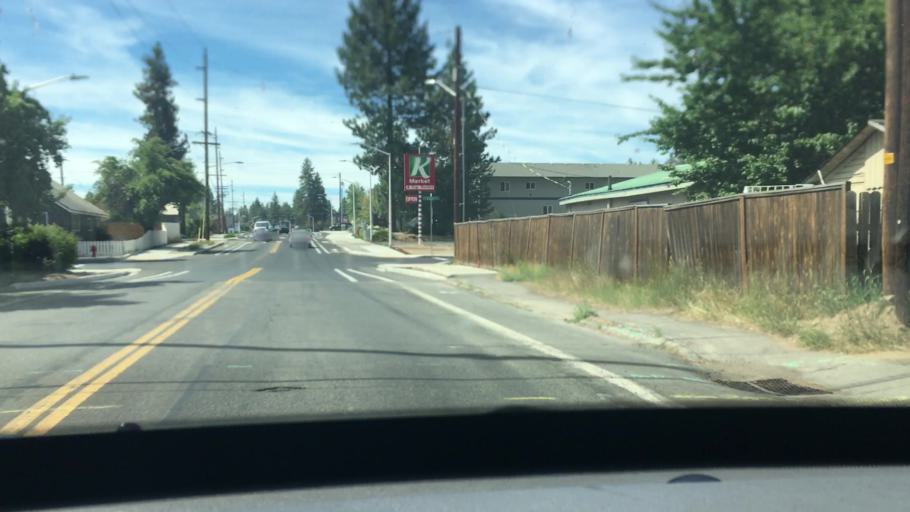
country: US
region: Oregon
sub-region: Deschutes County
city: Bend
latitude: 44.0523
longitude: -121.3318
